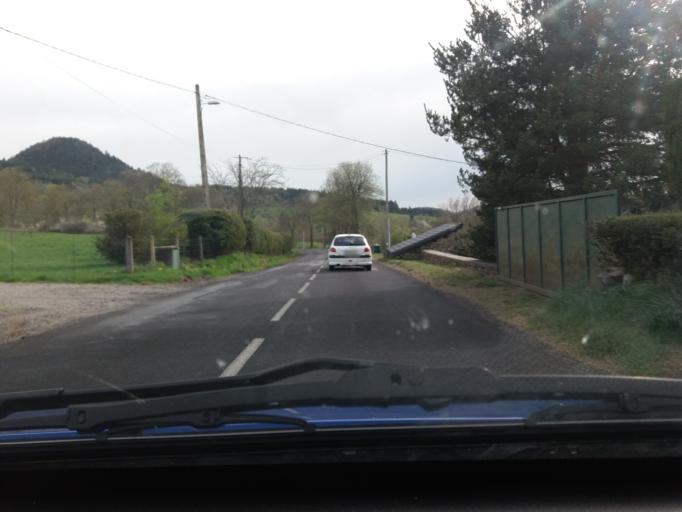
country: FR
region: Auvergne
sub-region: Departement de la Haute-Loire
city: Yssingeaux
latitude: 45.1267
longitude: 4.1563
